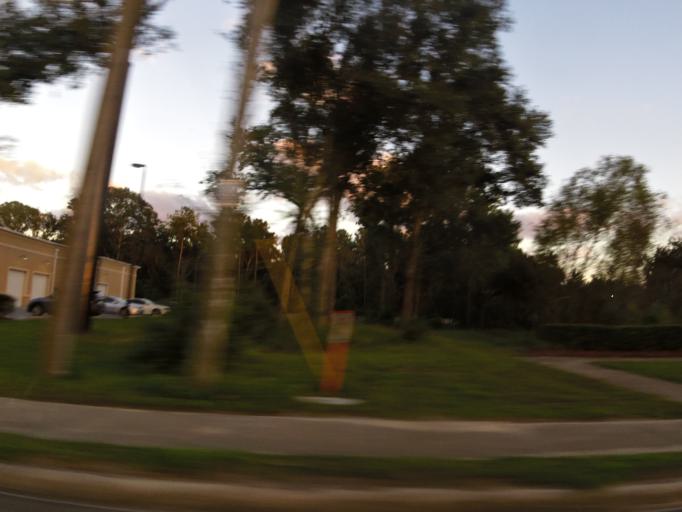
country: US
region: Florida
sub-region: Saint Johns County
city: Palm Valley
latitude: 30.0669
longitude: -81.4942
